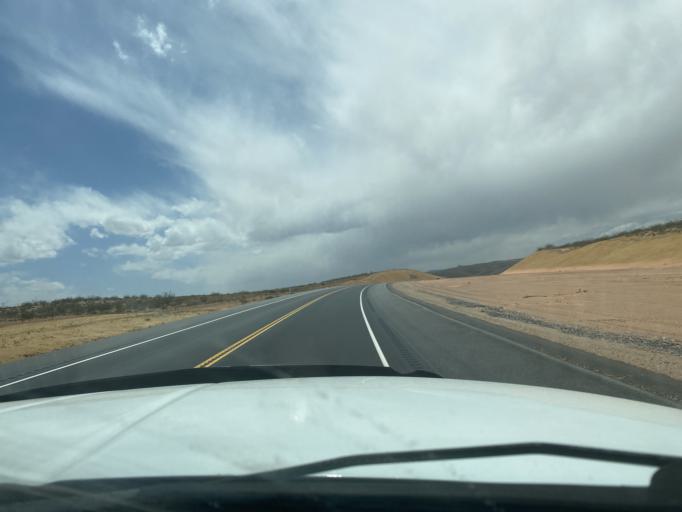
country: US
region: Utah
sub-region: Washington County
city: Hurricane
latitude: 37.1110
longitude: -113.3435
